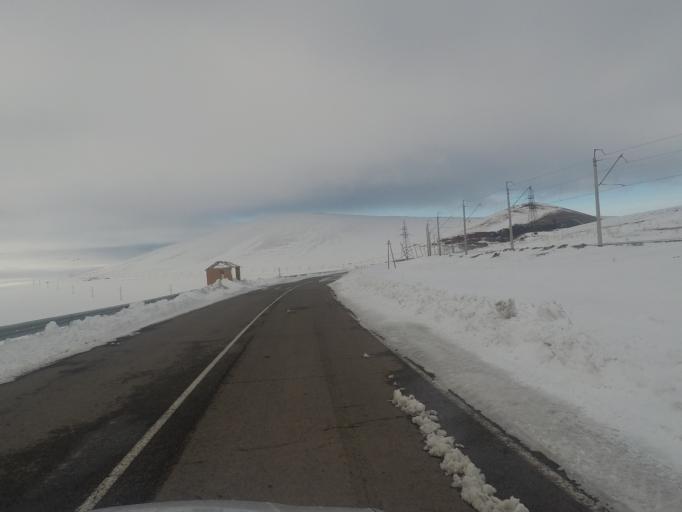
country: GE
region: Kvemo Kartli
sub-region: Tsalka
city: Tsalka
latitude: 41.4548
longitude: 43.8540
